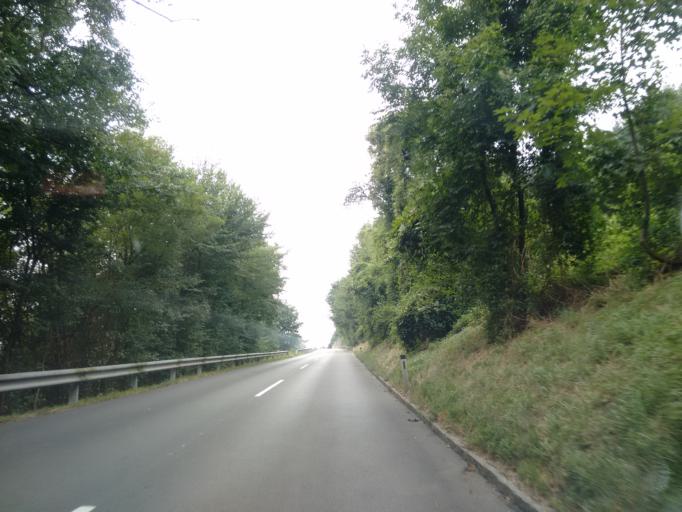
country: AT
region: Upper Austria
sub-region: Politischer Bezirk Grieskirchen
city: Bad Schallerbach
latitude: 48.2209
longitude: 13.8860
